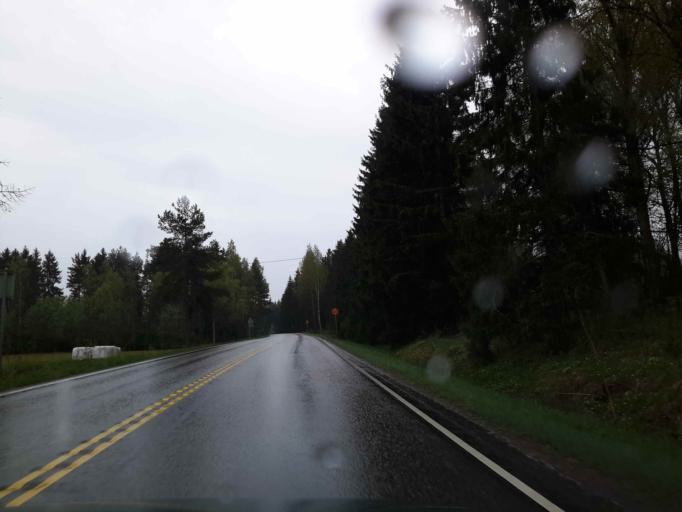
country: FI
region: Uusimaa
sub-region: Helsinki
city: Vihti
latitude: 60.3810
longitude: 24.5178
